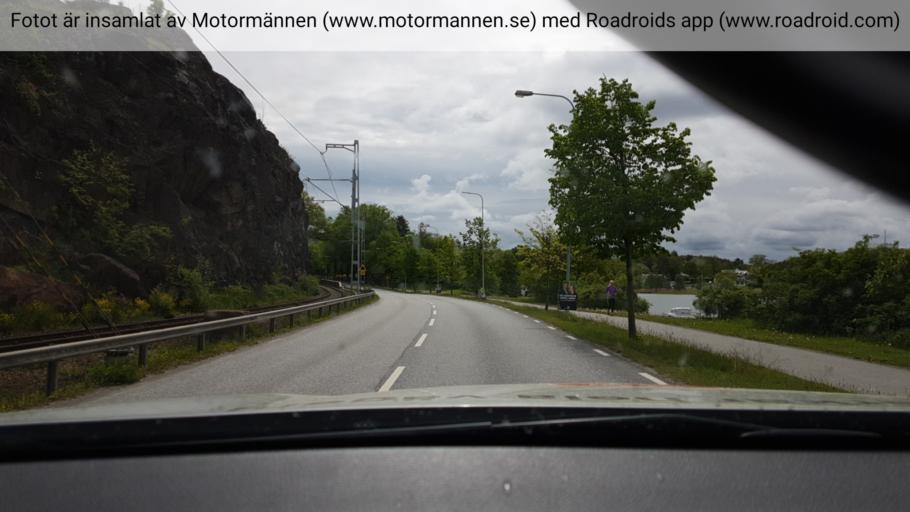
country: SE
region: Stockholm
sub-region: Nacka Kommun
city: Saltsjobaden
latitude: 59.2855
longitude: 18.2966
